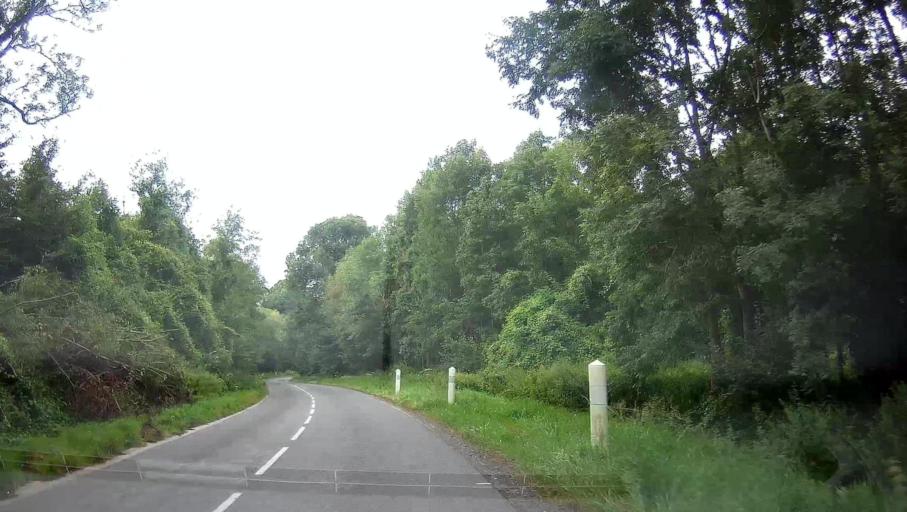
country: FR
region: Champagne-Ardenne
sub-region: Departement des Ardennes
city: Chateau-Porcien
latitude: 49.6198
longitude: 4.2323
